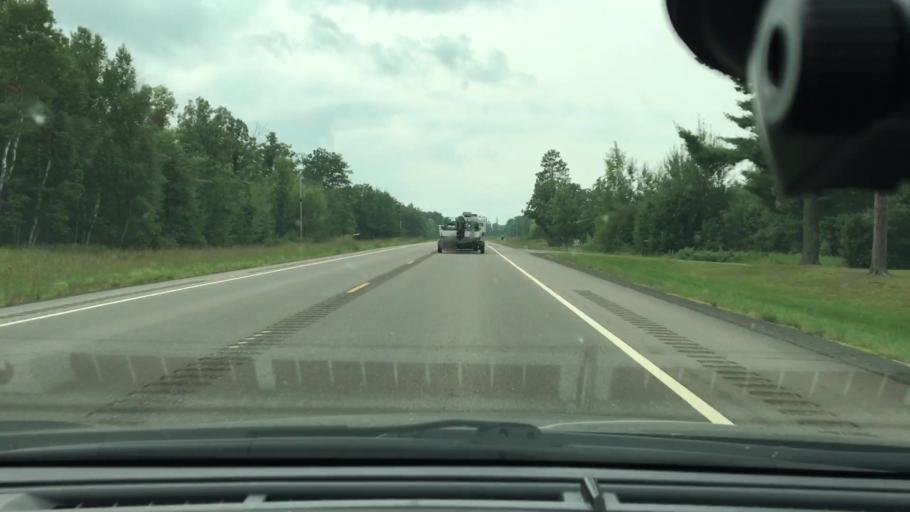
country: US
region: Minnesota
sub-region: Crow Wing County
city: Crosby
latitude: 46.5892
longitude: -93.9527
